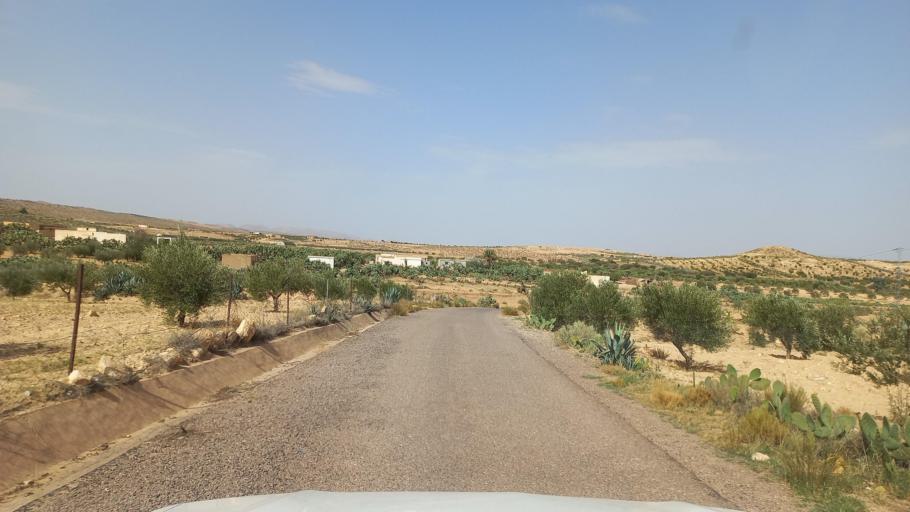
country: TN
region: Al Qasrayn
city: Kasserine
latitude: 35.2987
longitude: 8.9522
